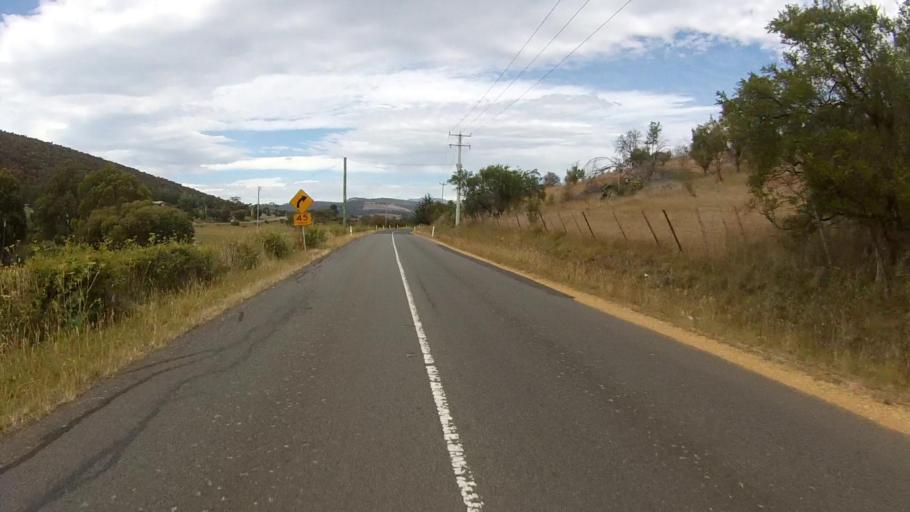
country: AU
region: Tasmania
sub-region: Clarence
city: Cambridge
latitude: -42.7390
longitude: 147.4226
